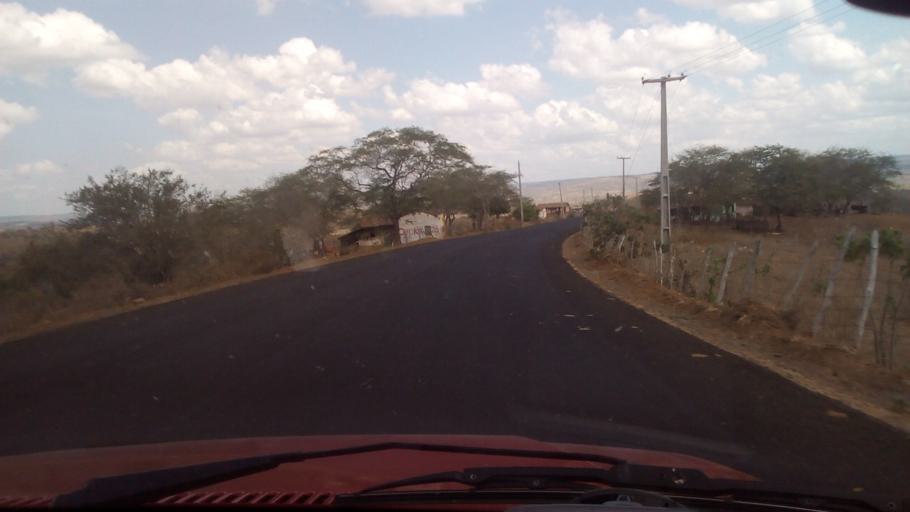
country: BR
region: Paraiba
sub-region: Cacimba De Dentro
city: Cacimba de Dentro
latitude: -6.6567
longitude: -35.7668
